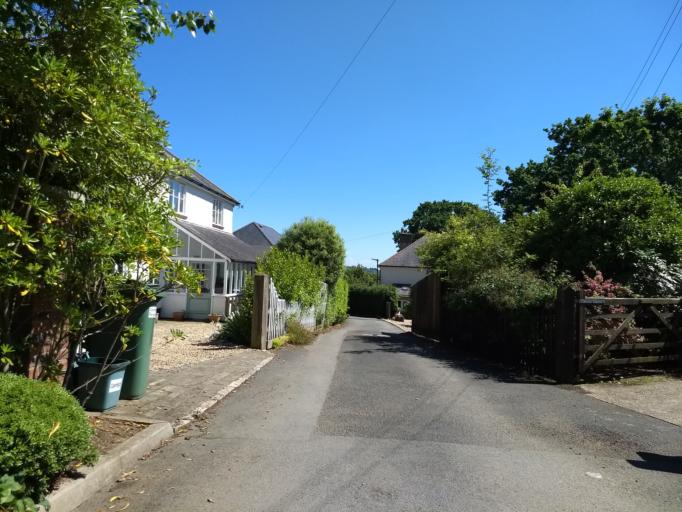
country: GB
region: England
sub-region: Isle of Wight
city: Seaview
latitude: 50.6963
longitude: -1.1112
